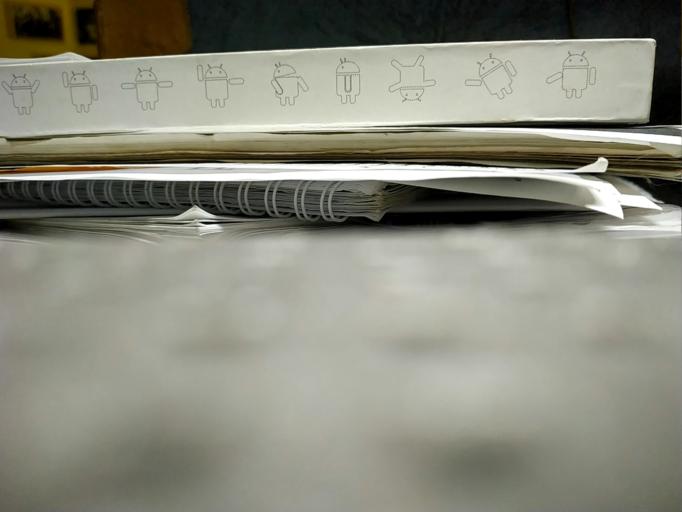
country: EE
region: Ida-Virumaa
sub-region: Narva-Joesuu linn
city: Narva-Joesuu
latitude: 59.6465
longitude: 27.9581
